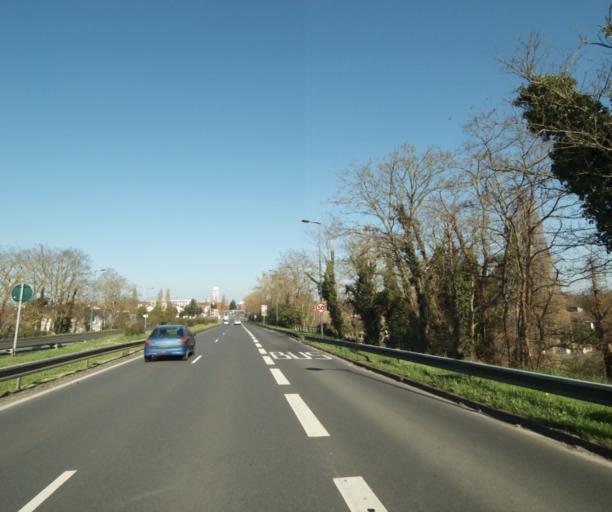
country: FR
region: Ile-de-France
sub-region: Departement du Val-d'Oise
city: Neuville-sur-Oise
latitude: 49.0286
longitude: 2.0670
